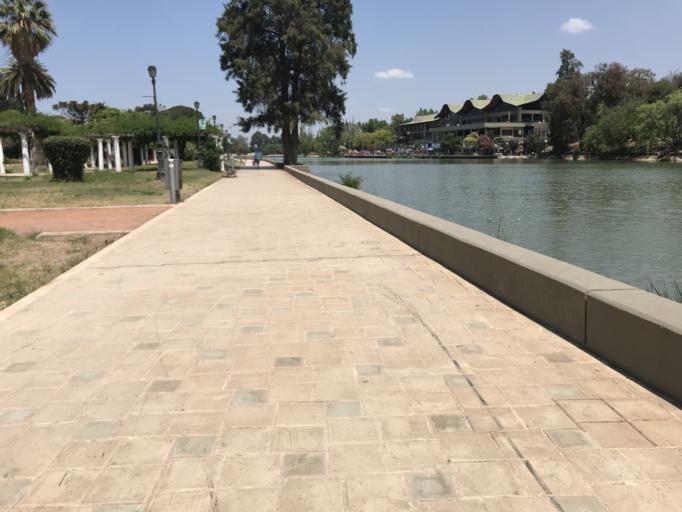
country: AR
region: Mendoza
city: Mendoza
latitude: -32.8913
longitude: -68.8671
